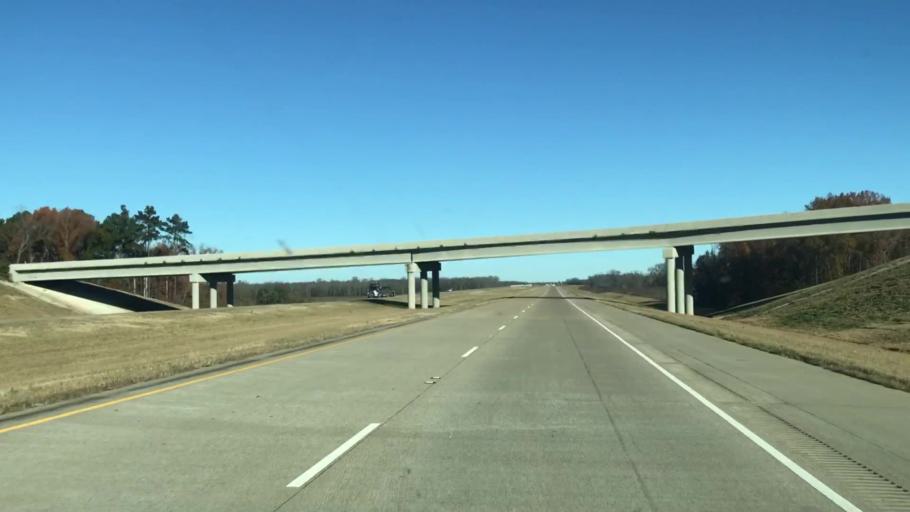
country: US
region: Louisiana
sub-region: Caddo Parish
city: Blanchard
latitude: 32.6154
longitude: -93.8348
